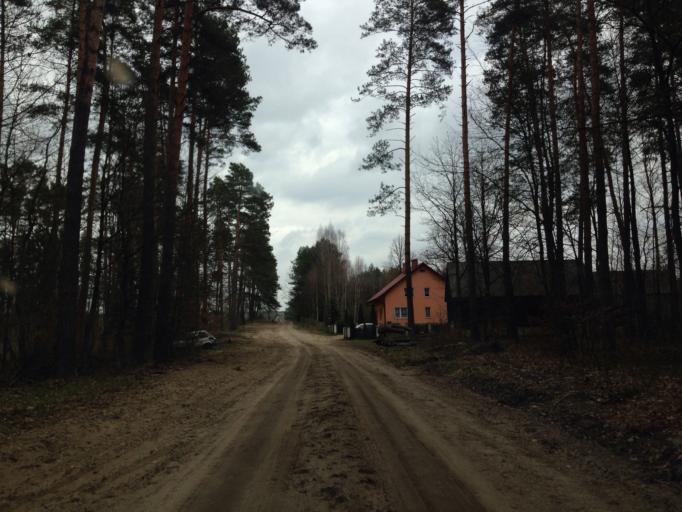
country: PL
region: Kujawsko-Pomorskie
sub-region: Powiat brodnicki
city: Gorzno
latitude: 53.2097
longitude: 19.7382
